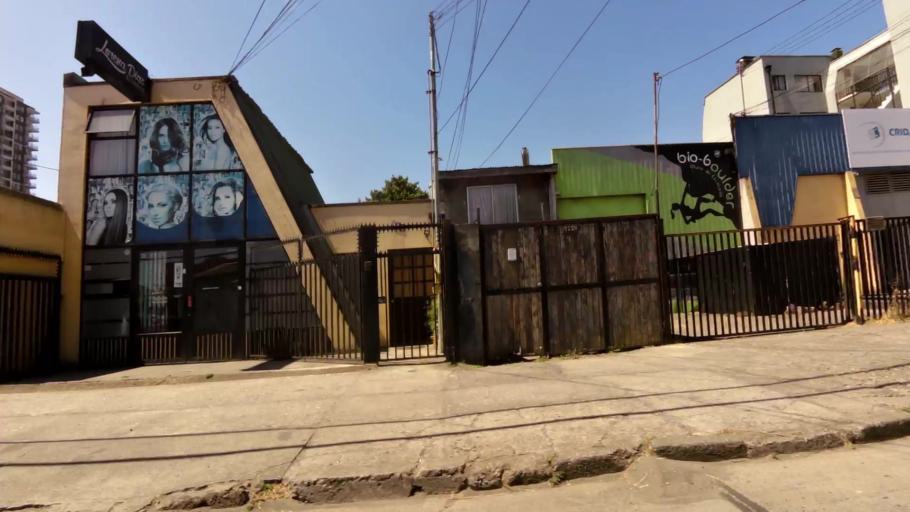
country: CL
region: Biobio
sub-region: Provincia de Concepcion
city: Concepcion
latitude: -36.8190
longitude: -73.0545
